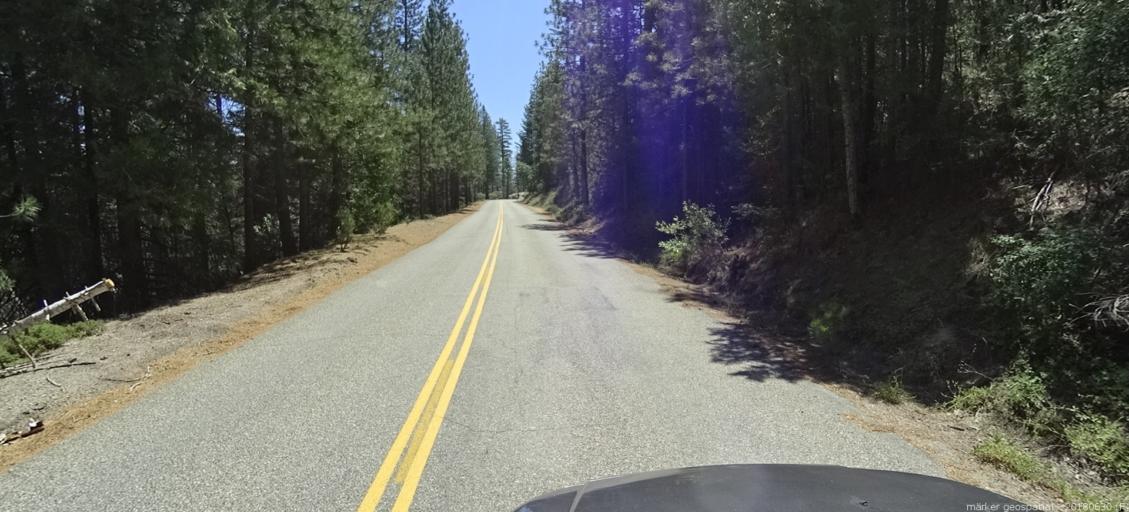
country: US
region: California
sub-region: Madera County
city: Oakhurst
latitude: 37.3546
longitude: -119.3864
